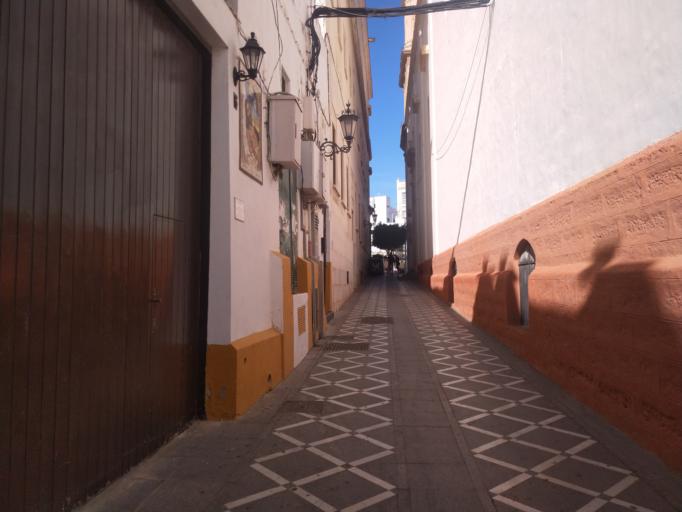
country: ES
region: Andalusia
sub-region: Provincia de Cadiz
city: San Fernando
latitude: 36.4654
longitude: -6.1960
